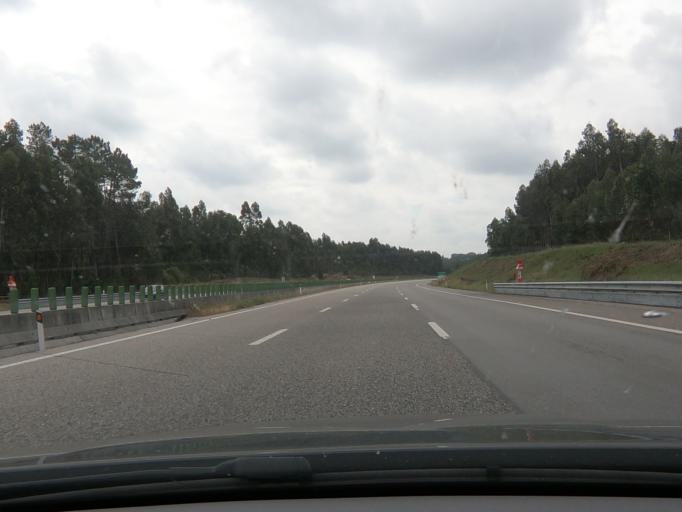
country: PT
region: Leiria
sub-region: Pombal
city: Lourical
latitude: 39.9852
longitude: -8.7904
